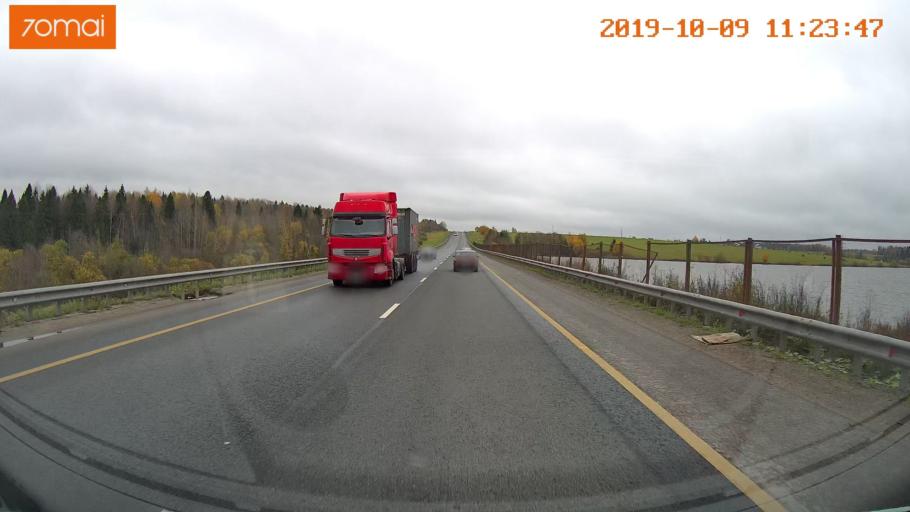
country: RU
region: Vologda
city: Vologda
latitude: 59.1174
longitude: 39.9735
